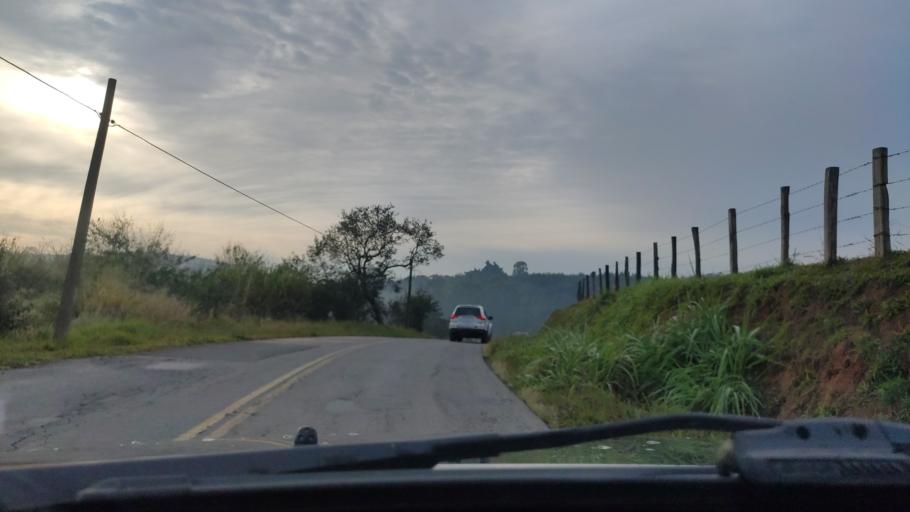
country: BR
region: Sao Paulo
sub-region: Jarinu
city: Jarinu
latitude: -23.1335
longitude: -46.7806
